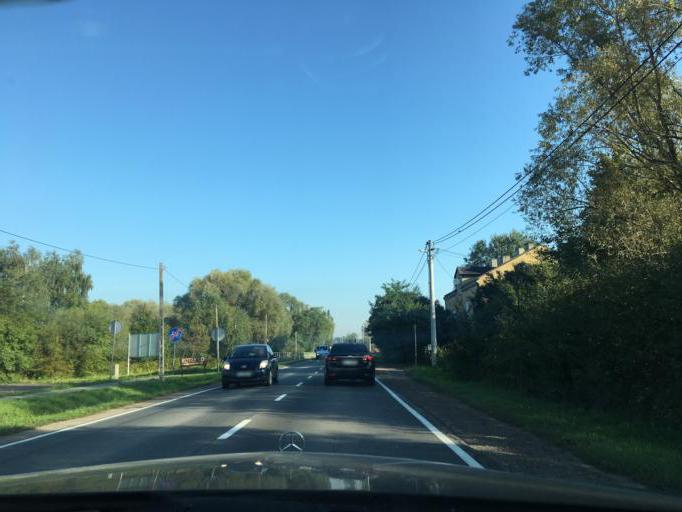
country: PL
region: Masovian Voivodeship
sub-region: Powiat grodziski
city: Grodzisk Mazowiecki
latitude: 52.1392
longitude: 20.6168
